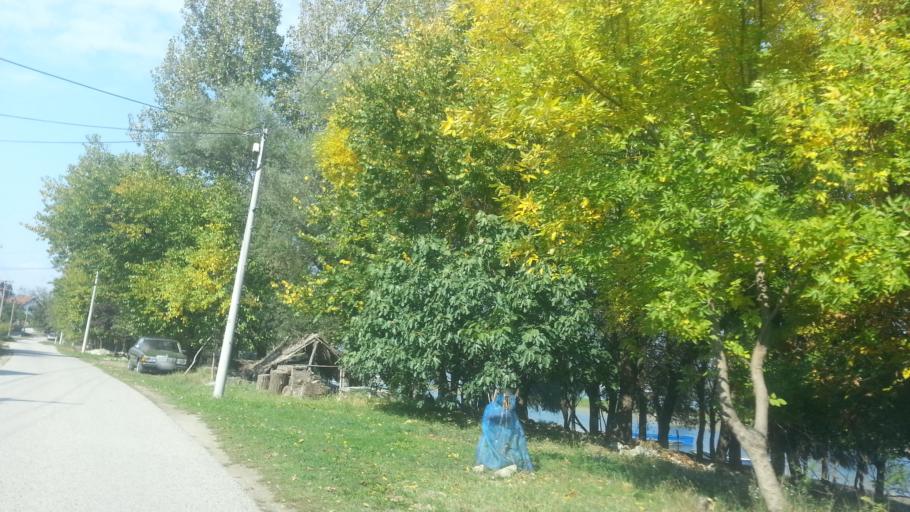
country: RS
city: Novi Slankamen
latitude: 45.1497
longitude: 20.2487
